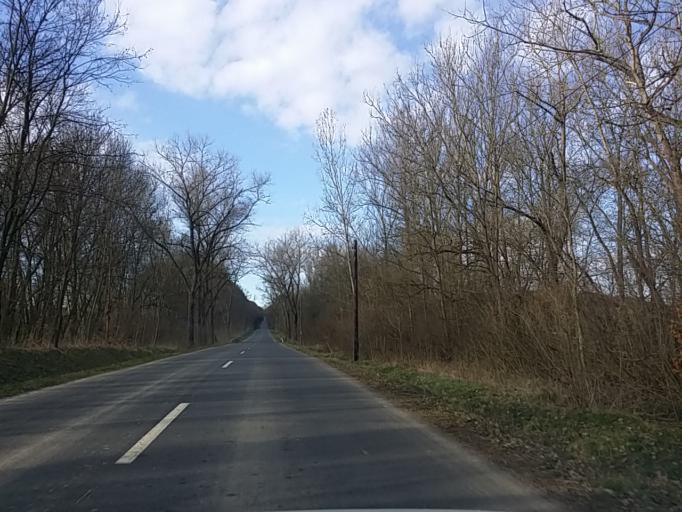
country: HU
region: Borsod-Abauj-Zemplen
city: Rudabanya
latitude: 48.4632
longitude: 20.4962
